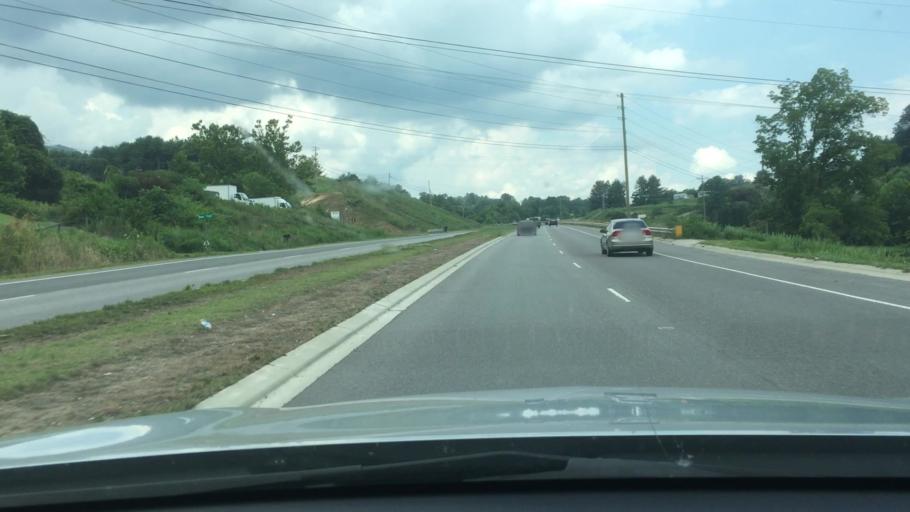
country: US
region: North Carolina
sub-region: Yancey County
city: Burnsville
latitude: 35.9122
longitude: -82.3454
